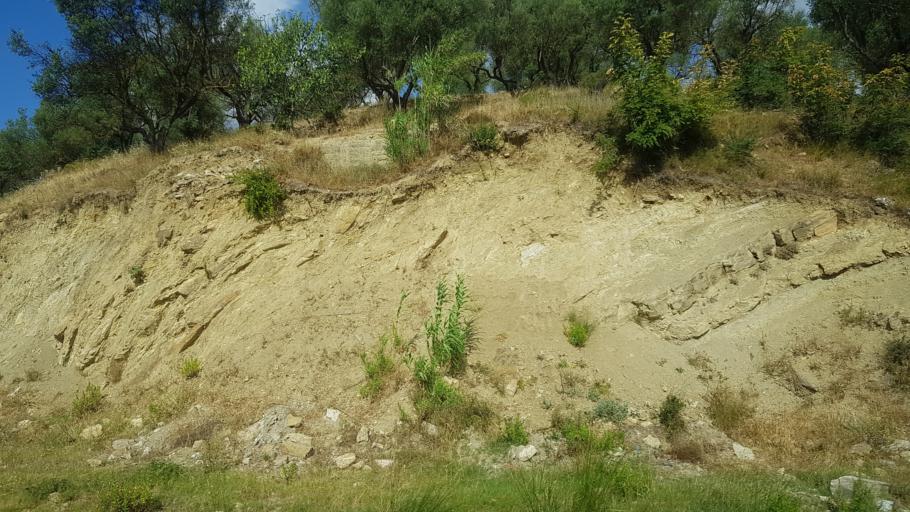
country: AL
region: Vlore
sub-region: Rrethi i Delvines
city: Mesopotam
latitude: 39.9016
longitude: 20.0857
